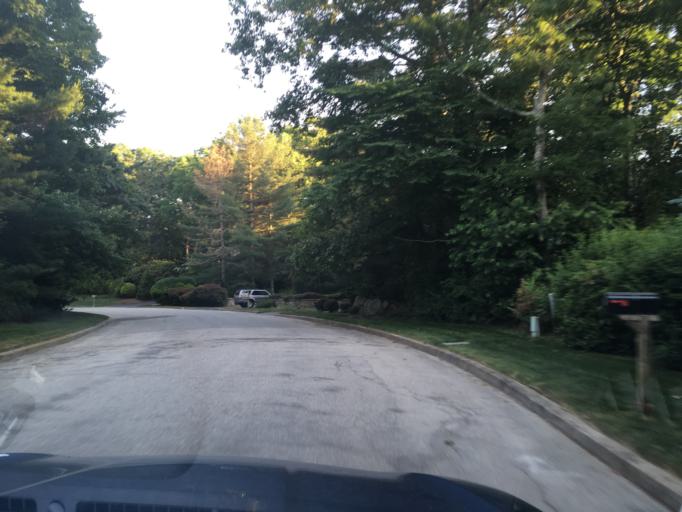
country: US
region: Rhode Island
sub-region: Kent County
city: West Warwick
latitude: 41.6364
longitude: -71.5208
